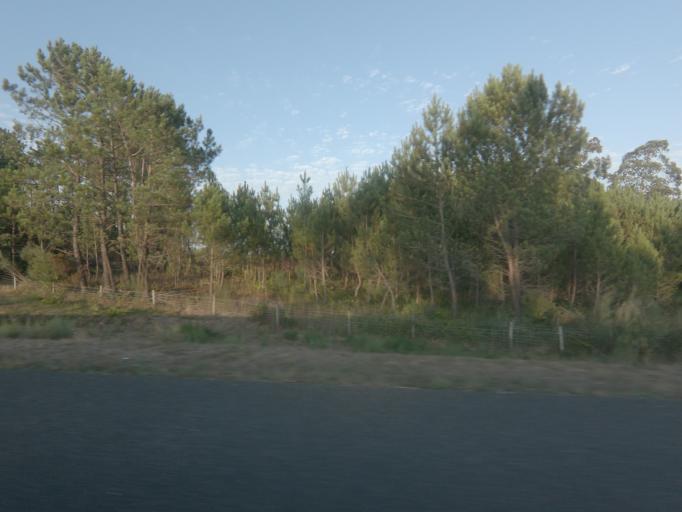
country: PT
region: Leiria
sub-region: Leiria
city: Santa Catarina da Serra
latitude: 39.6521
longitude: -8.6960
